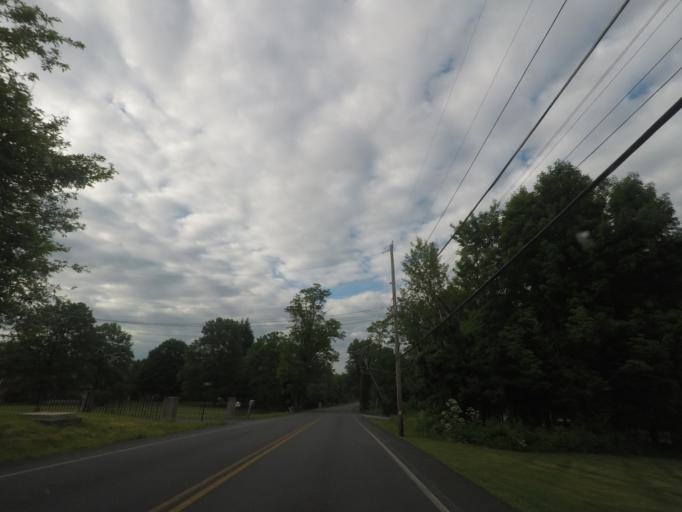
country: US
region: New York
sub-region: Ulster County
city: Plattekill
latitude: 41.6019
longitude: -74.1172
